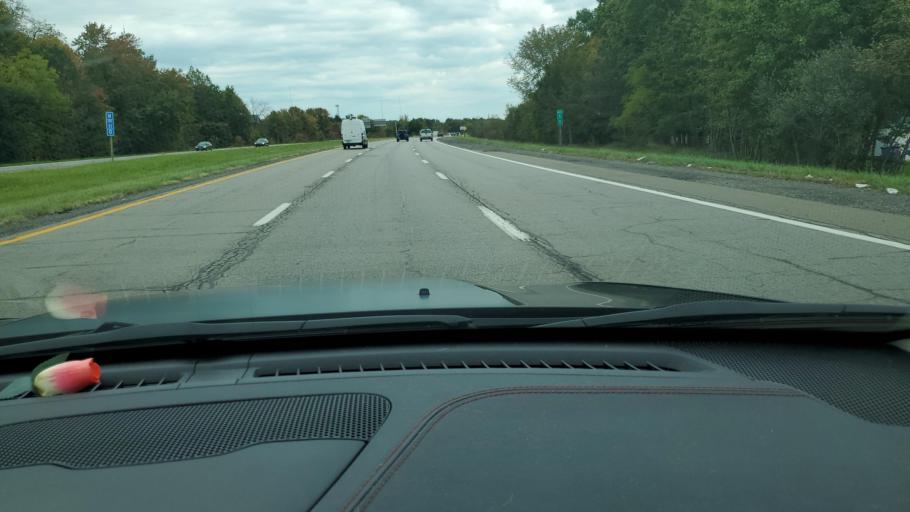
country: US
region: Ohio
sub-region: Mahoning County
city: Poland
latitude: 41.0350
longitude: -80.6310
